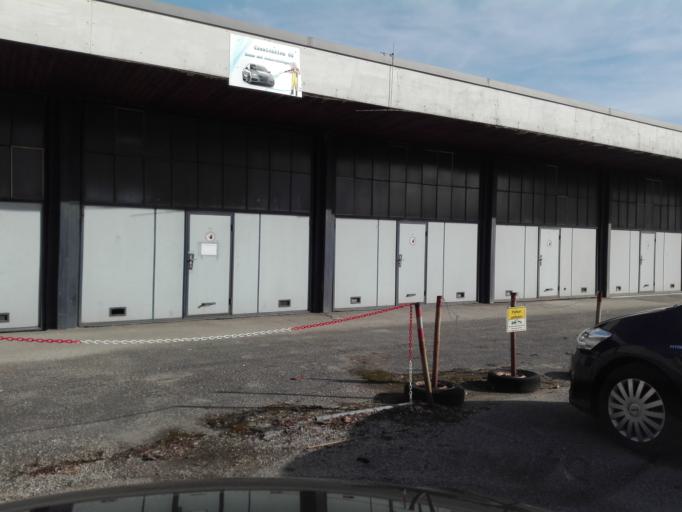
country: AT
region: Upper Austria
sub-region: Politischer Bezirk Perg
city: Perg
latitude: 48.2488
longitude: 14.6403
